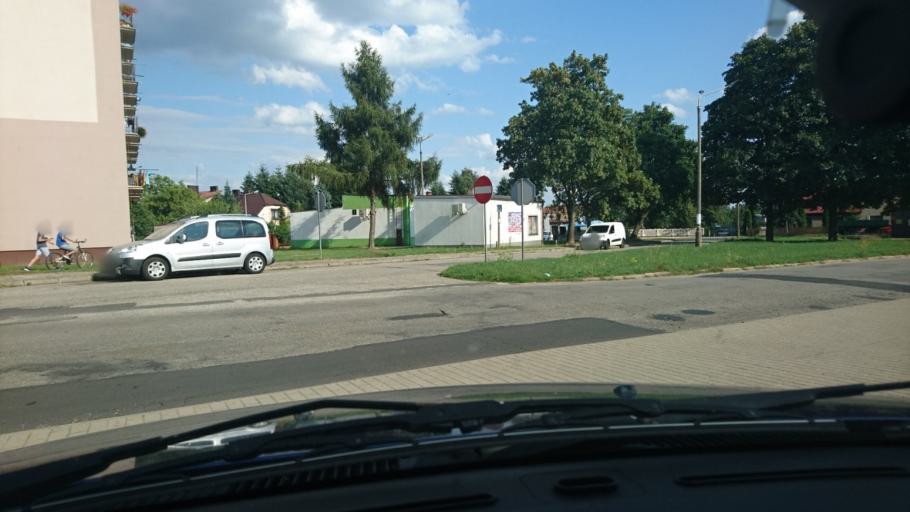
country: PL
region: Greater Poland Voivodeship
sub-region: Powiat ostrowski
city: Odolanow
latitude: 51.5784
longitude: 17.6602
